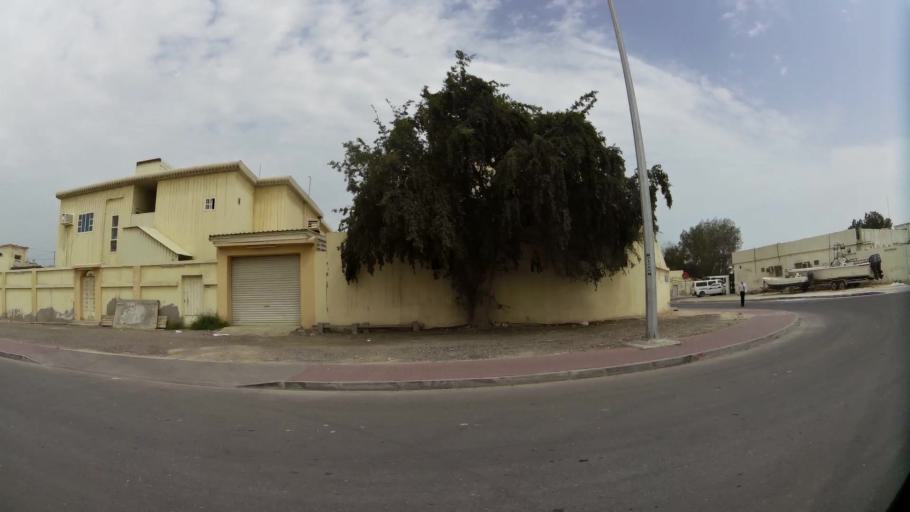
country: QA
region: Baladiyat ar Rayyan
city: Ar Rayyan
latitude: 25.3294
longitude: 51.4685
